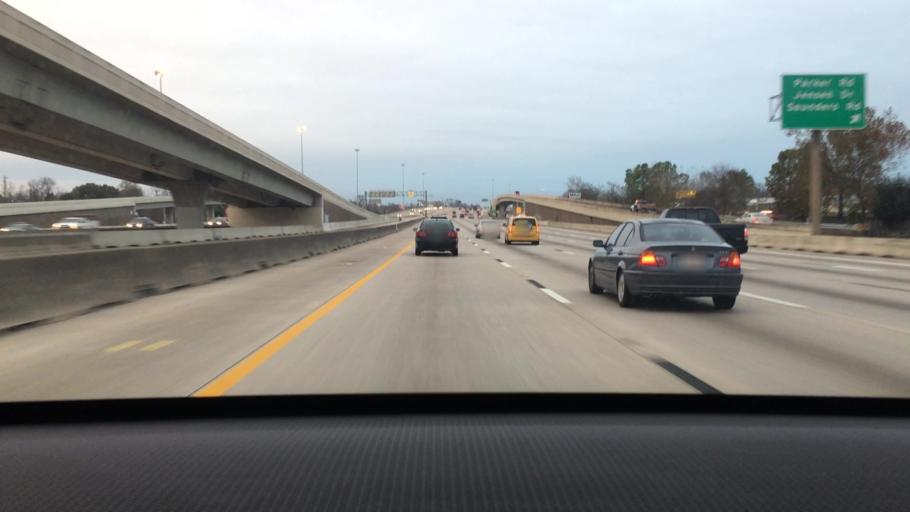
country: US
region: Texas
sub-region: Harris County
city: Houston
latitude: 29.8516
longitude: -95.3335
